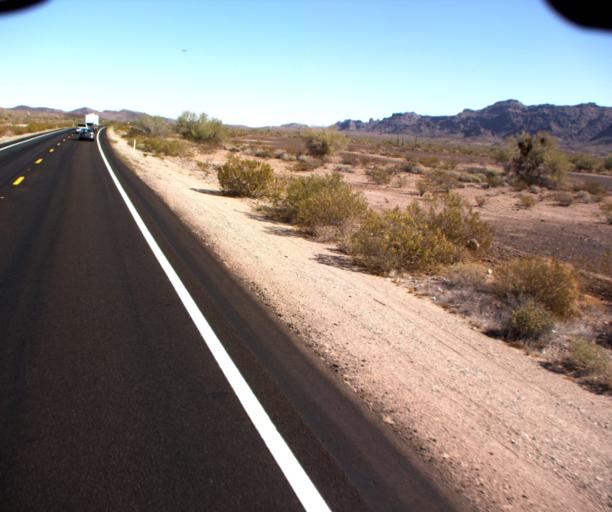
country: US
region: Arizona
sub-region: La Paz County
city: Quartzsite
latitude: 33.1857
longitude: -114.2749
